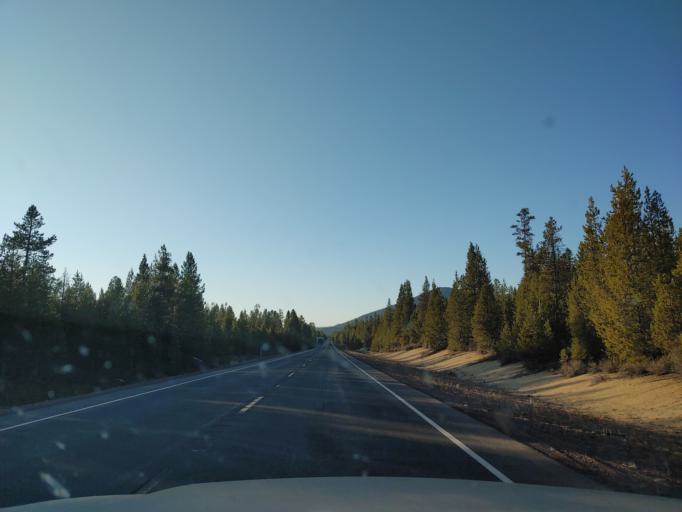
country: US
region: Oregon
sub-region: Deschutes County
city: La Pine
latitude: 43.4021
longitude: -121.8226
